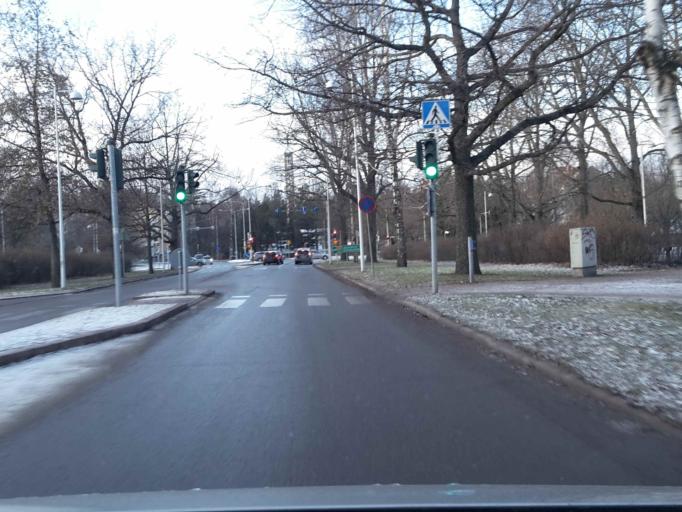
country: FI
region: Uusimaa
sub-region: Helsinki
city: Teekkarikylae
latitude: 60.1581
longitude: 24.8765
